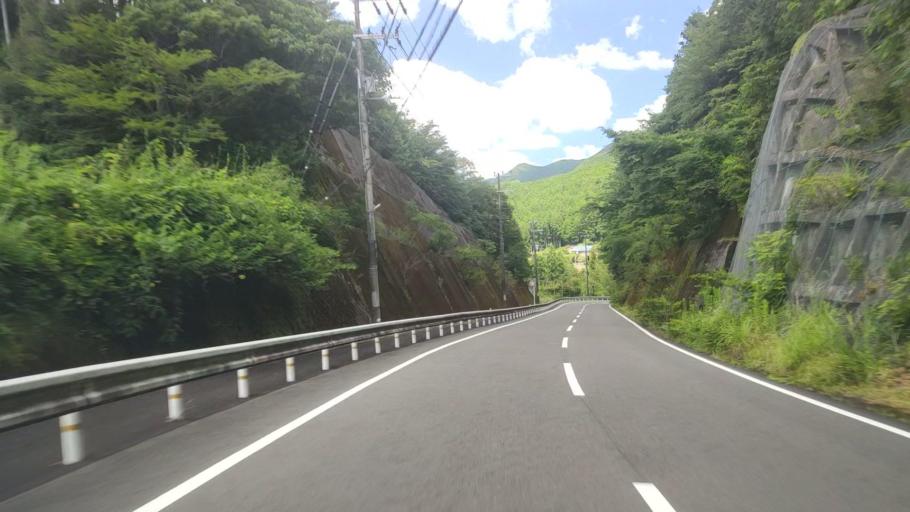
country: JP
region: Mie
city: Owase
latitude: 33.9547
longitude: 136.0689
